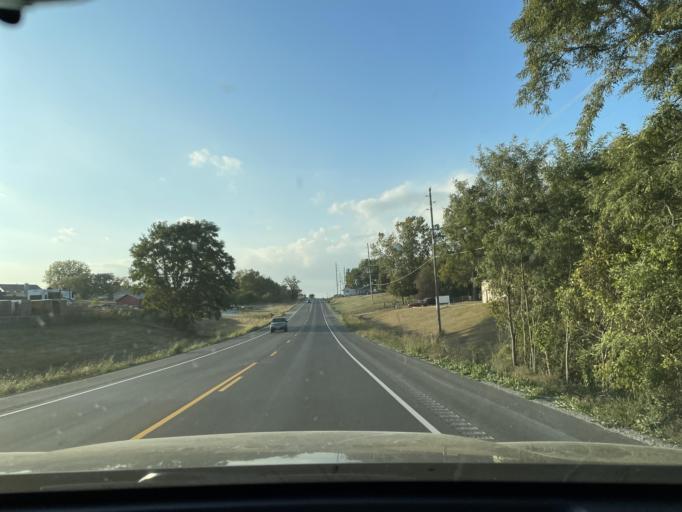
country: US
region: Missouri
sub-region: Andrew County
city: Country Club Village
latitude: 39.8269
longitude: -94.8563
